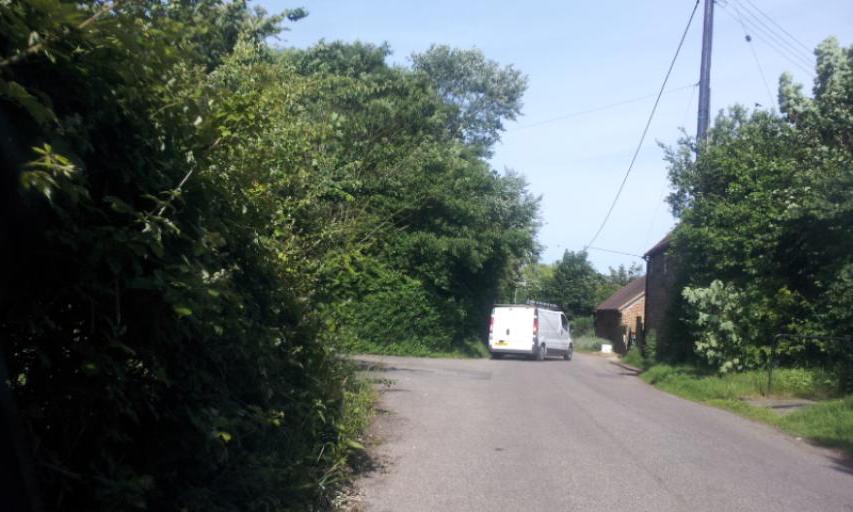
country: GB
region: England
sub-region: Kent
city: Leysdown-on-Sea
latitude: 51.4149
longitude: 0.8972
